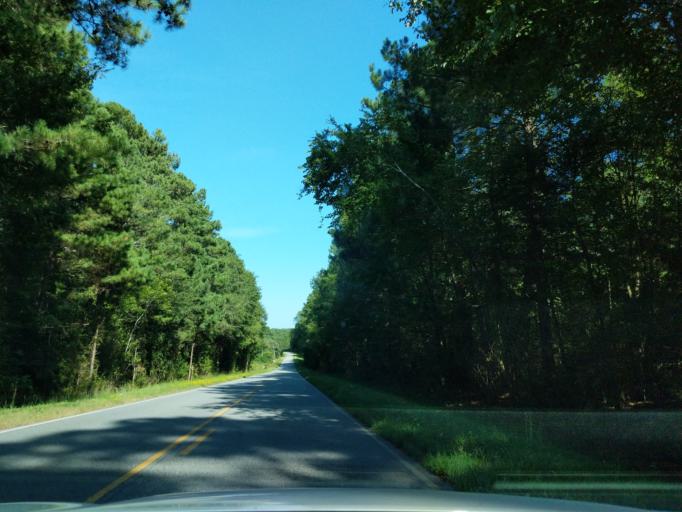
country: US
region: Georgia
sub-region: Madison County
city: Comer
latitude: 33.9741
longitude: -83.0968
